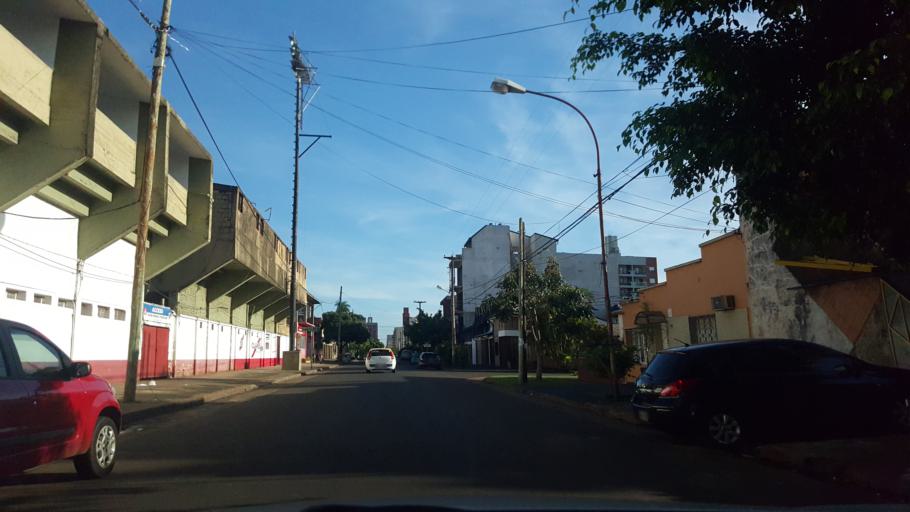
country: AR
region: Misiones
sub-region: Departamento de Capital
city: Posadas
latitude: -27.3565
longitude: -55.8964
